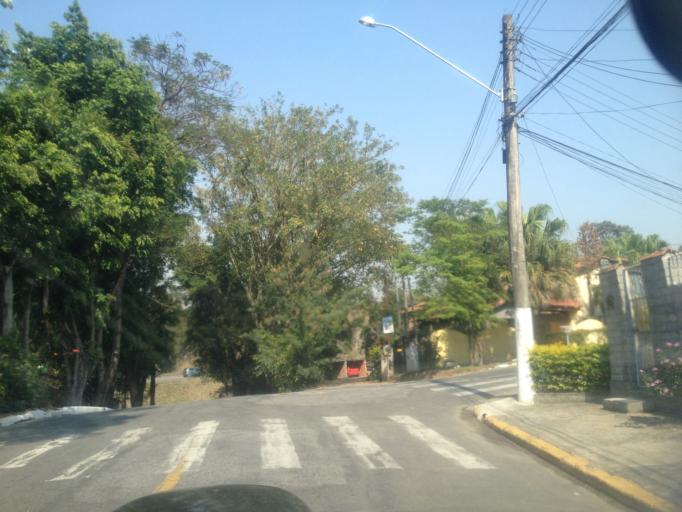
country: BR
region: Rio de Janeiro
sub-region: Porto Real
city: Porto Real
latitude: -22.4513
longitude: -44.3061
